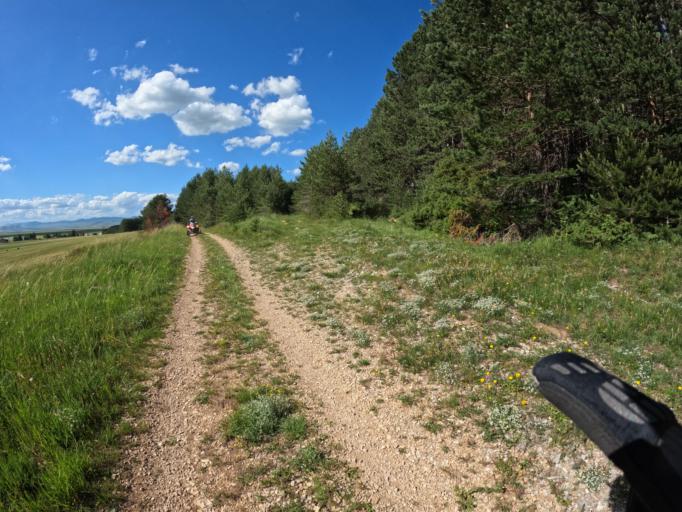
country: BA
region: Federation of Bosnia and Herzegovina
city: Glamoc
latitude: 44.0732
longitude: 16.8551
